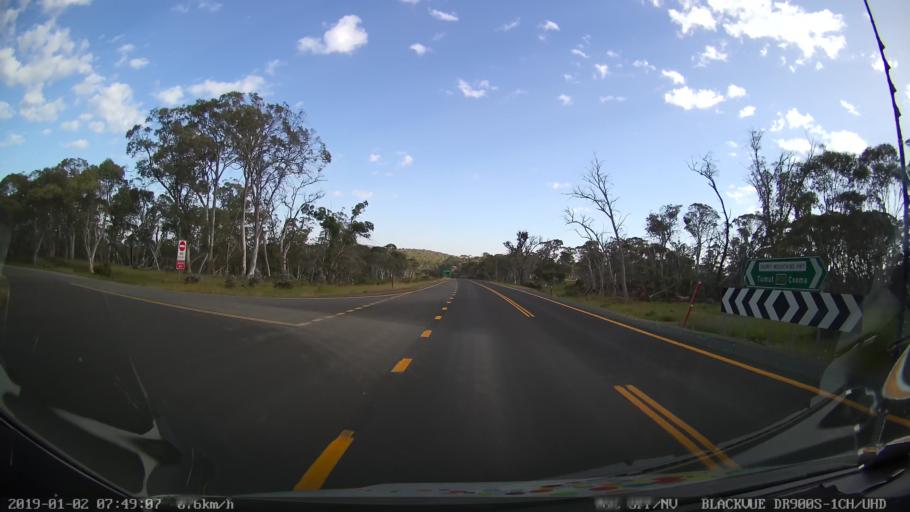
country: AU
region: New South Wales
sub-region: Tumut Shire
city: Tumut
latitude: -35.7455
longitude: 148.5214
